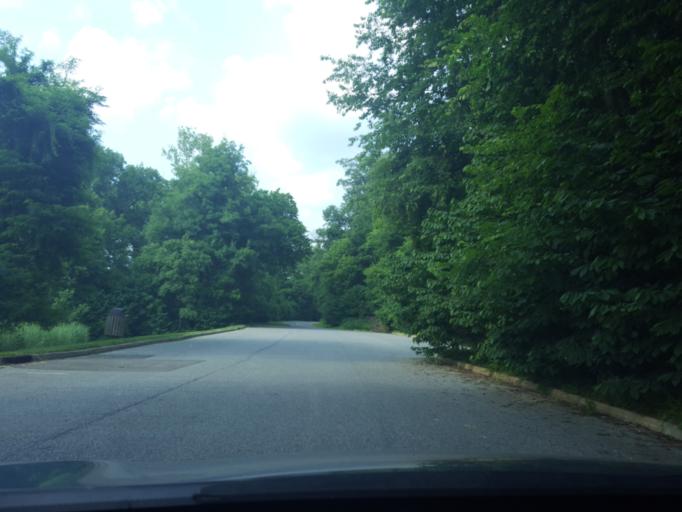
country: US
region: Maryland
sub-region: Prince George's County
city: Fort Washington
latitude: 38.7134
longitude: -77.0340
